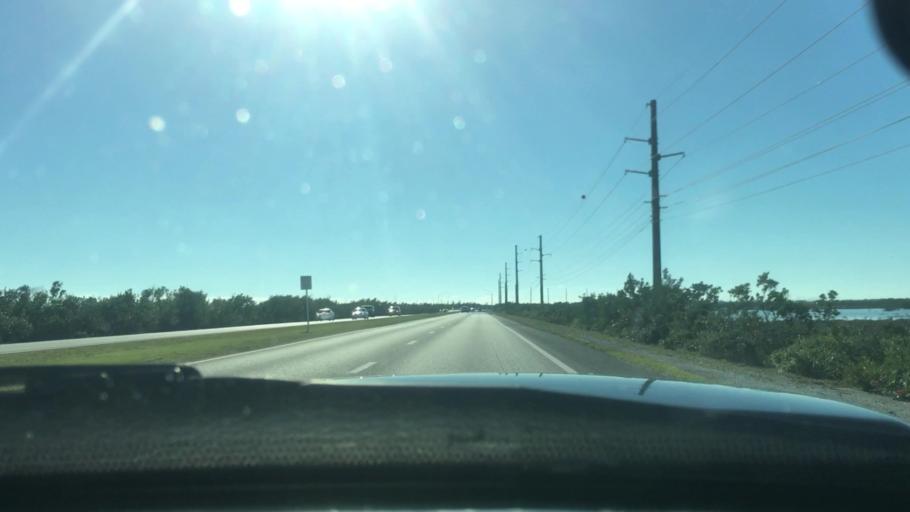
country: US
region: Florida
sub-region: Monroe County
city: Stock Island
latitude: 24.5840
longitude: -81.7008
